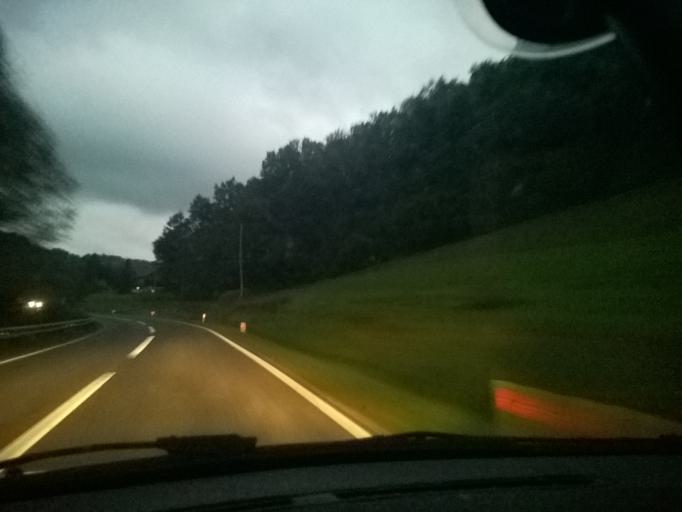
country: SI
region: Rogatec
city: Rogatec
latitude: 46.2205
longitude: 15.7361
